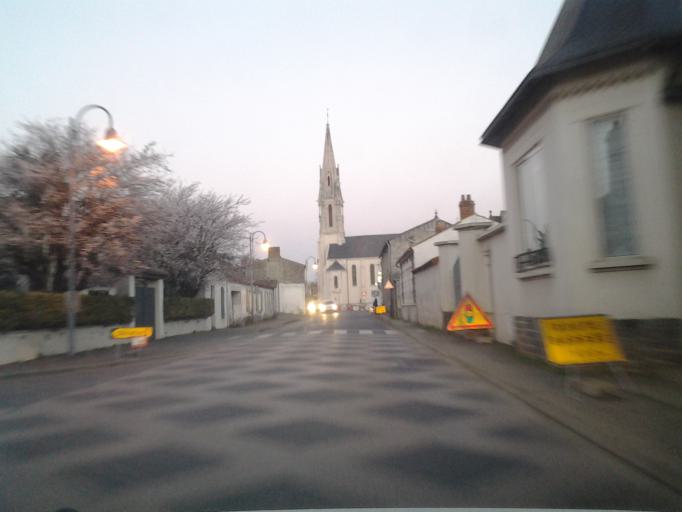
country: FR
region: Pays de la Loire
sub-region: Departement de la Vendee
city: Saint-Gervais
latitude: 46.9025
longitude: -2.0023
